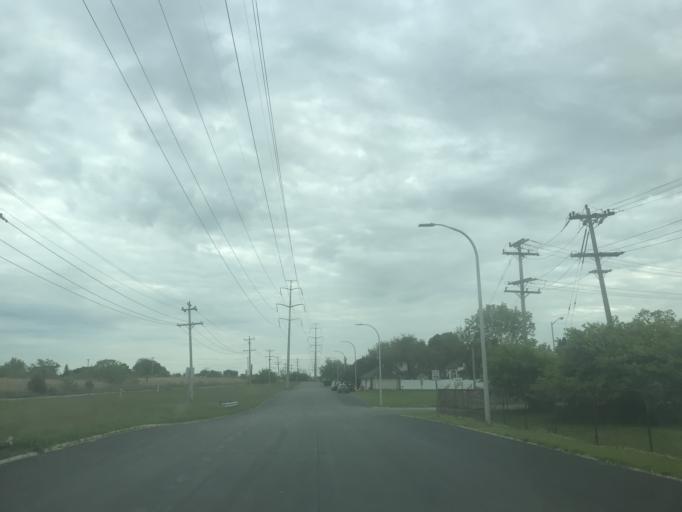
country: US
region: Michigan
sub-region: Wayne County
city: Riverview
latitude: 42.1805
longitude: -83.1694
